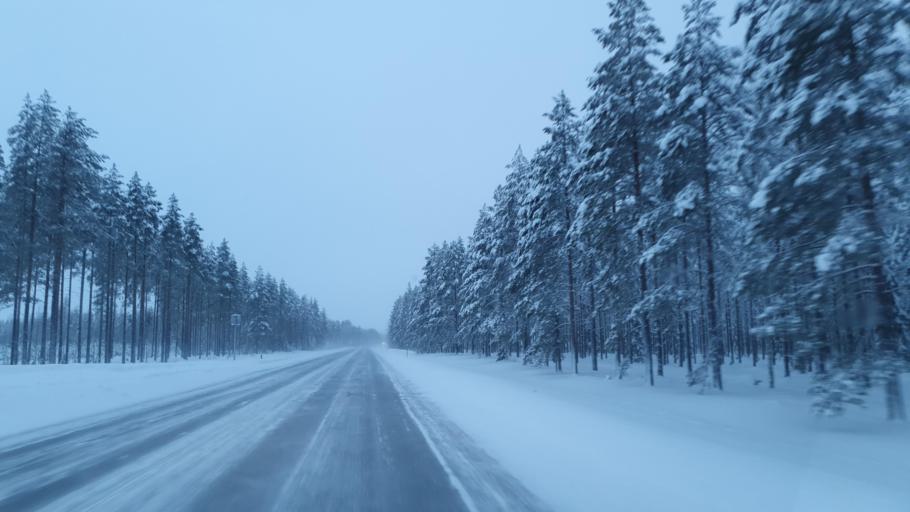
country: FI
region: Kainuu
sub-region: Kajaani
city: Vaala
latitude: 64.5538
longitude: 27.0467
